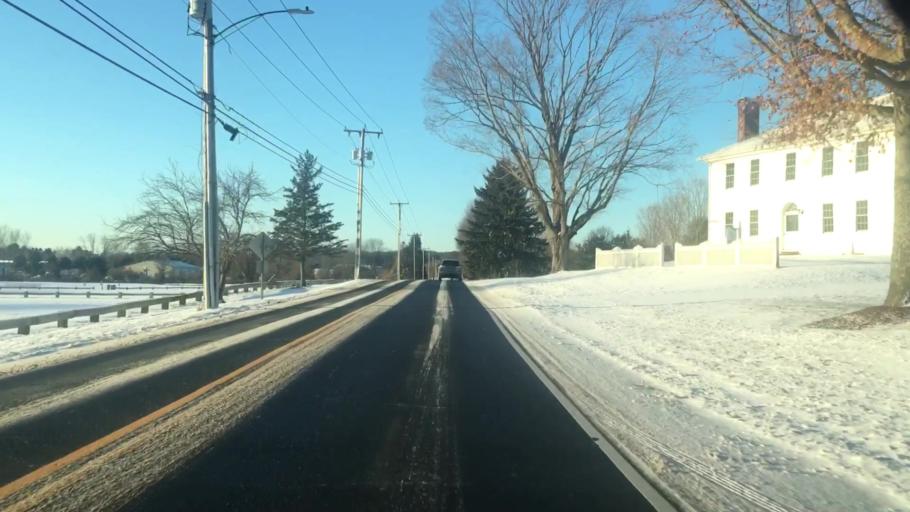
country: US
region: Connecticut
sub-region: Tolland County
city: Ellington
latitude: 41.8770
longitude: -72.4855
